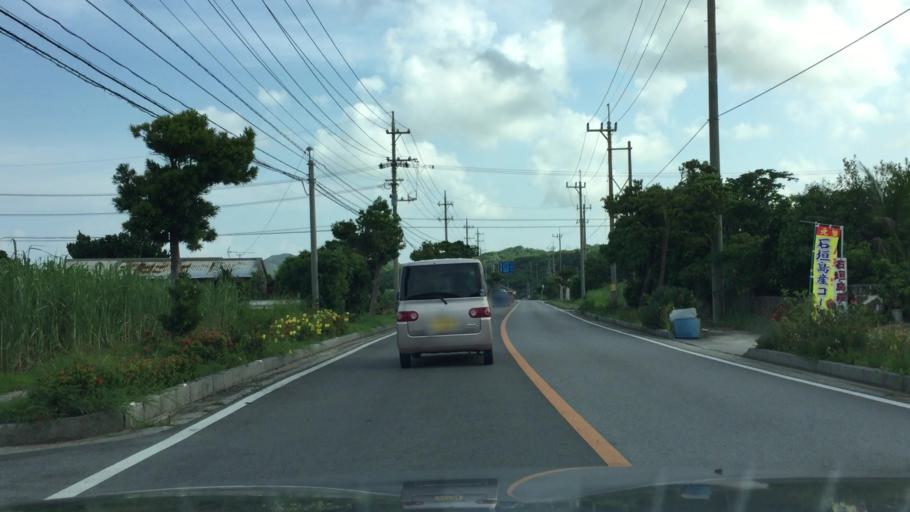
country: JP
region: Okinawa
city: Ishigaki
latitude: 24.4359
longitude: 124.2490
